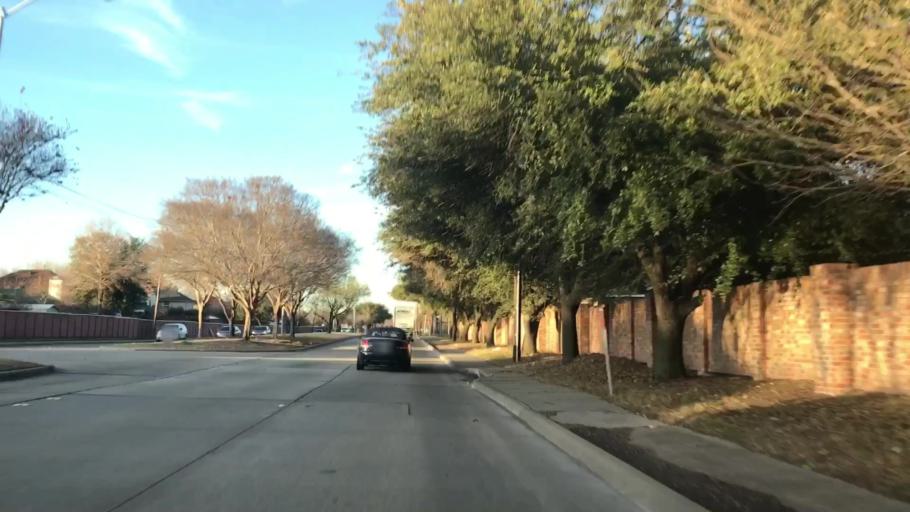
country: US
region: Texas
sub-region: Dallas County
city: Rowlett
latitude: 32.9023
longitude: -96.5180
